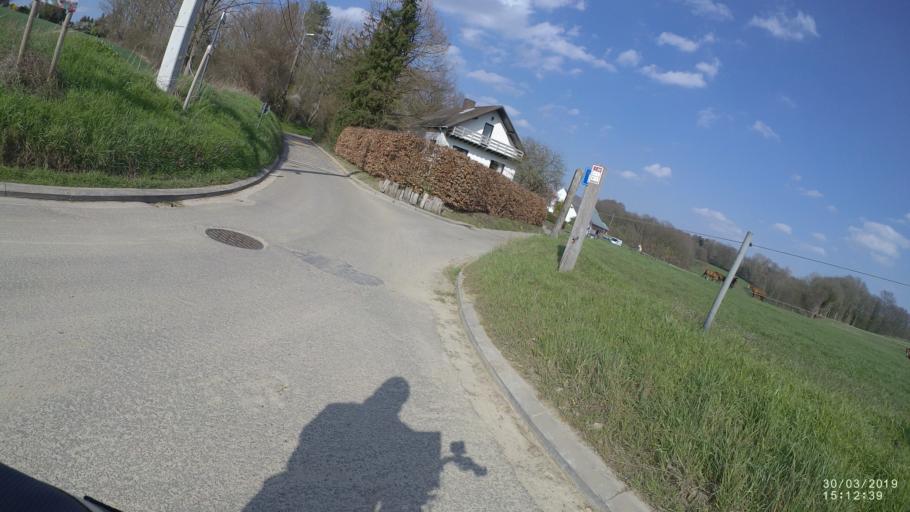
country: BE
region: Flanders
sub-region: Provincie Vlaams-Brabant
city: Overijse
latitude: 50.7577
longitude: 4.5507
